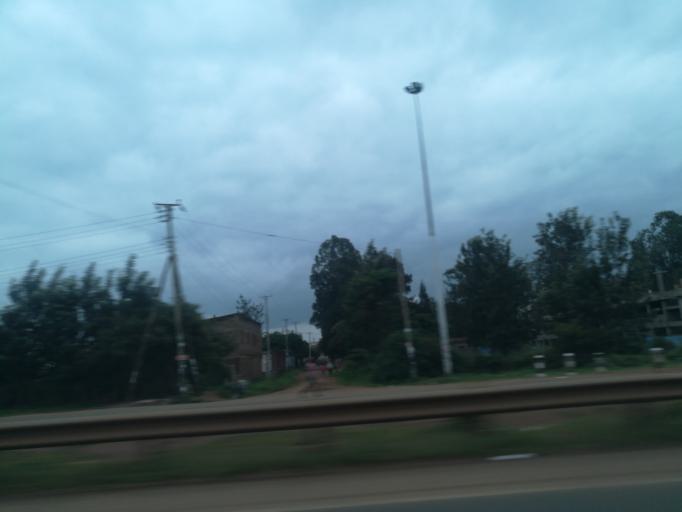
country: KE
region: Nairobi Area
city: Thika
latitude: -1.0987
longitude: 37.0243
